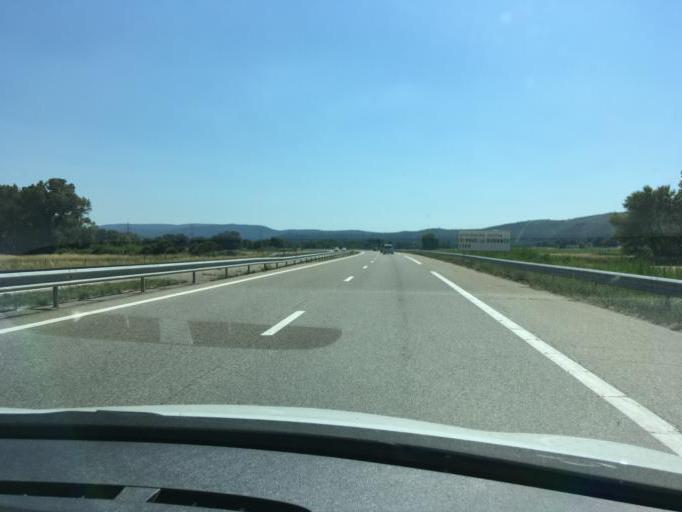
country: FR
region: Provence-Alpes-Cote d'Azur
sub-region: Departement du Vaucluse
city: Beaumont-de-Pertuis
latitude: 43.7291
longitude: 5.7424
